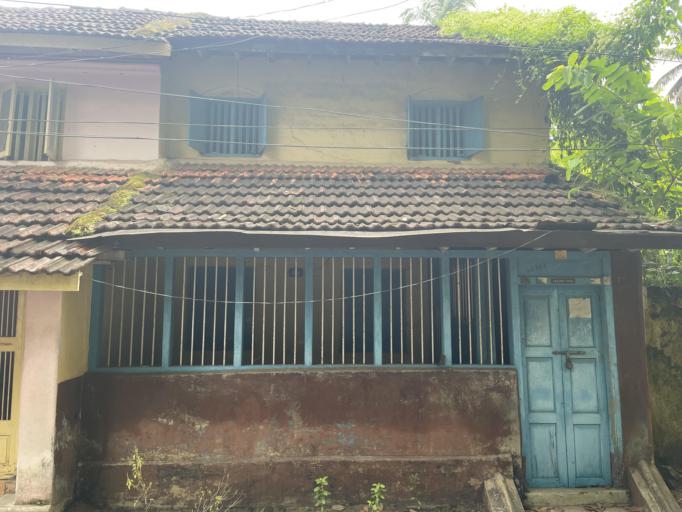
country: IN
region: Kerala
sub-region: Palakkad district
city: Chittur
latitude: 10.6935
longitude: 76.7410
